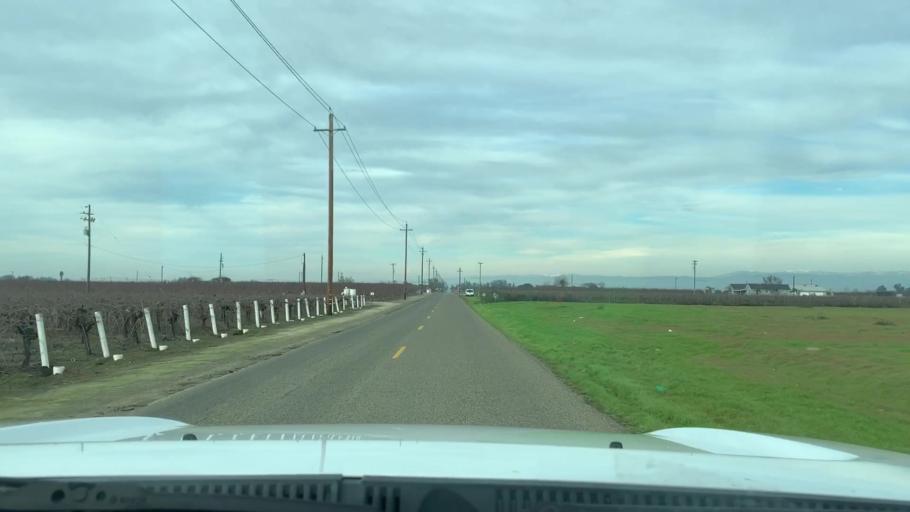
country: US
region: California
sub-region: Fresno County
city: Selma
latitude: 36.5862
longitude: -119.5749
